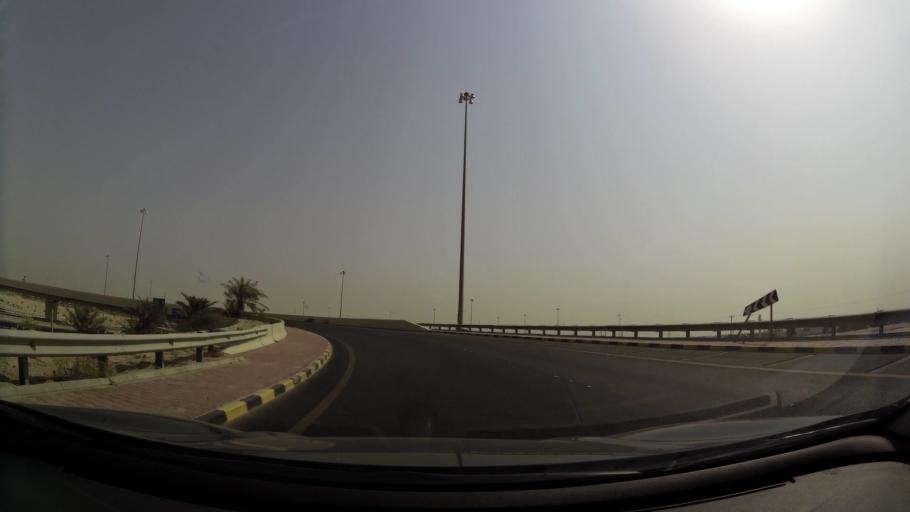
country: KW
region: Muhafazat al Jahra'
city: Al Jahra'
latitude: 29.2959
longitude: 47.7295
